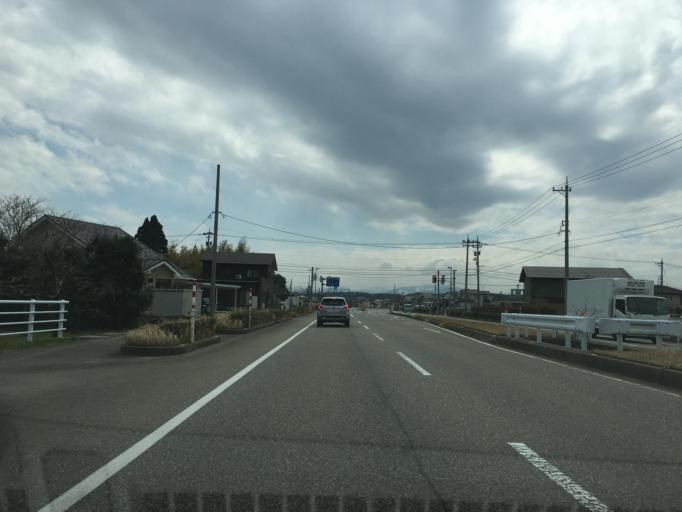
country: JP
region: Toyama
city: Kuragaki-kosugi
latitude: 36.7044
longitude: 137.1151
